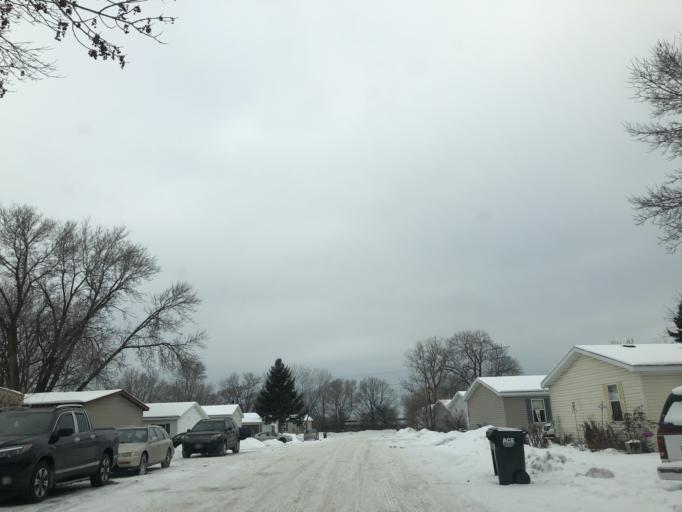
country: US
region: Minnesota
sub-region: Ramsey County
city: New Brighton
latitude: 45.0848
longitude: -93.1842
